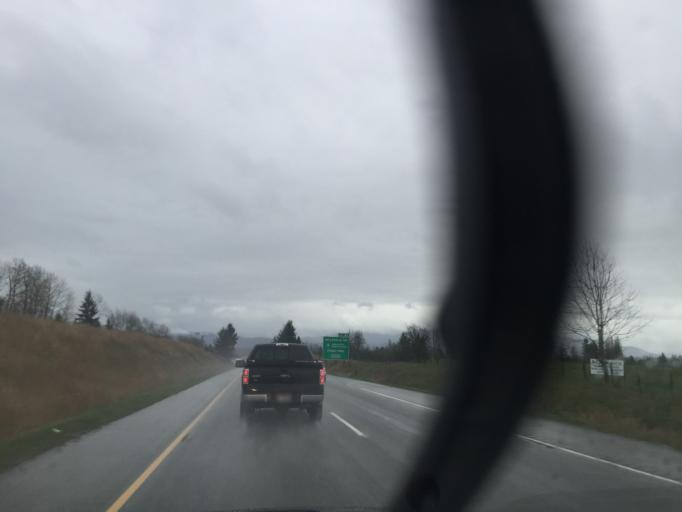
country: CA
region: British Columbia
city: Aldergrove
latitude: 49.0658
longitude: -122.4024
